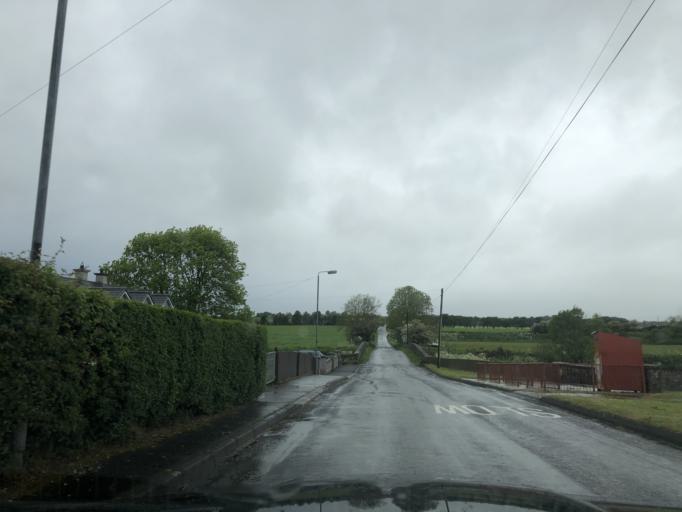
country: GB
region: Northern Ireland
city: Dunloy
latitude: 55.1235
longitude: -6.3630
